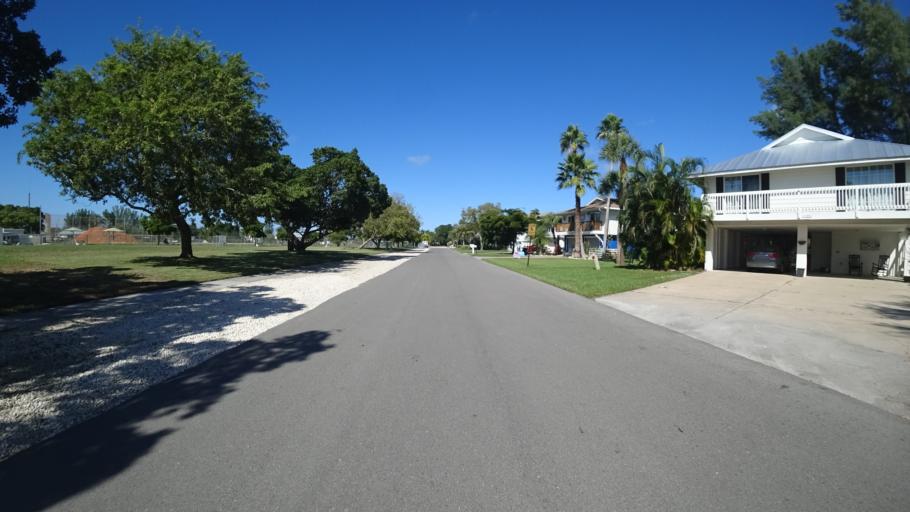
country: US
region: Florida
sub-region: Manatee County
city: Holmes Beach
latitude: 27.5106
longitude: -82.7137
